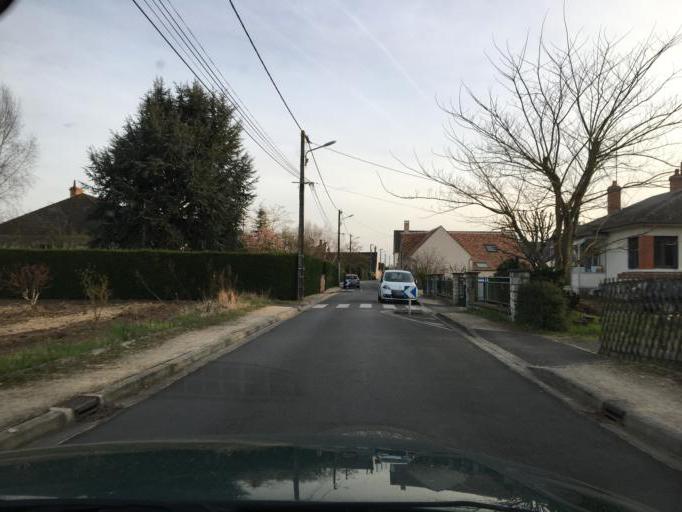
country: FR
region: Centre
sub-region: Departement du Loiret
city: Olivet
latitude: 47.8621
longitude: 1.8867
